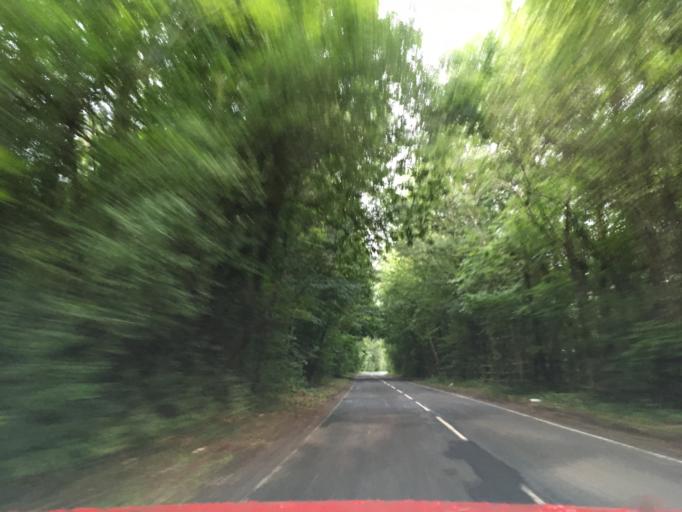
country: GB
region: Wales
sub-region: Newport
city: Langstone
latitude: 51.6281
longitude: -2.8968
